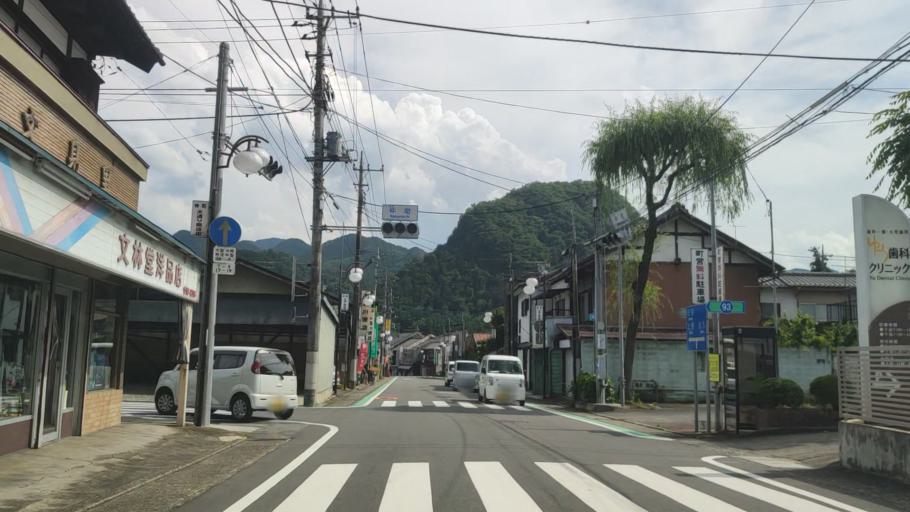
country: JP
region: Gunma
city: Tomioka
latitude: 36.2118
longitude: 138.7827
